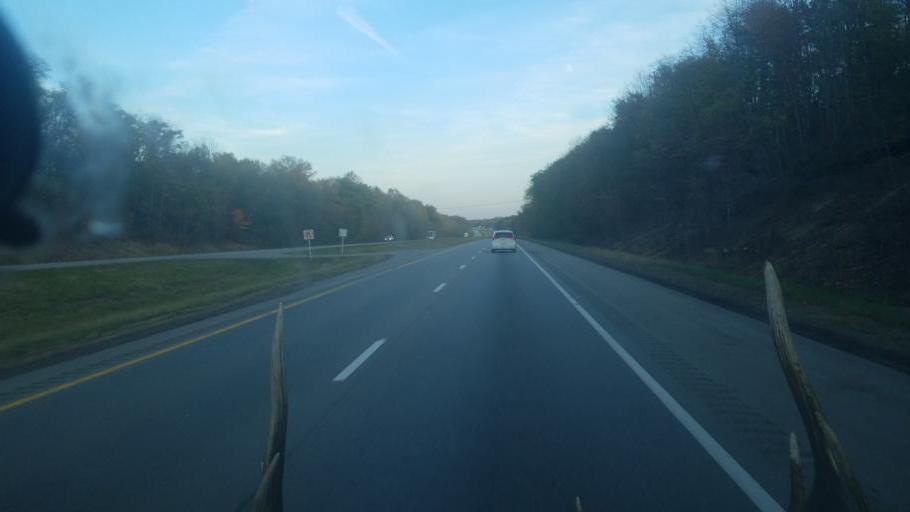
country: US
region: Ohio
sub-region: Muskingum County
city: Zanesville
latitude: 39.9493
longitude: -82.1649
